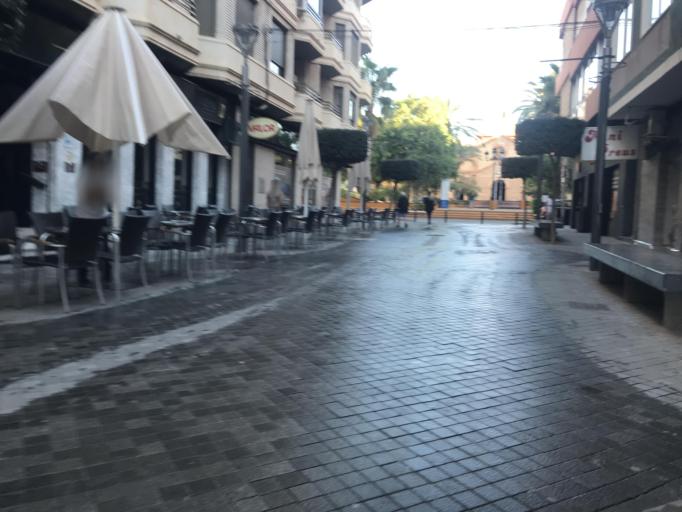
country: ES
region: Valencia
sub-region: Provincia de Alicante
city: Torrevieja
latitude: 37.9767
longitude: -0.6827
